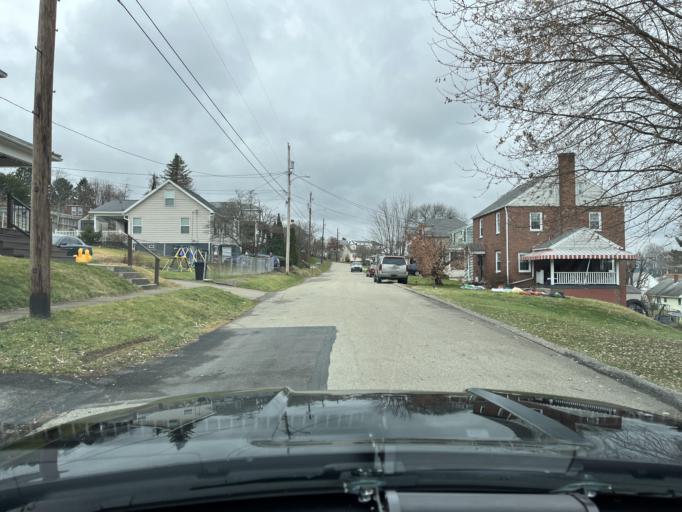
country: US
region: Pennsylvania
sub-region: Fayette County
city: South Uniontown
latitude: 39.8914
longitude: -79.7462
